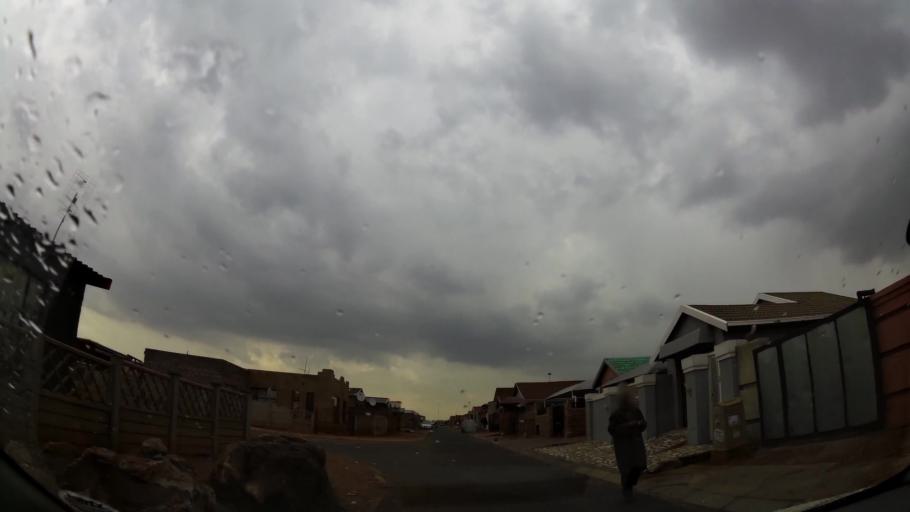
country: ZA
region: Gauteng
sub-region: Ekurhuleni Metropolitan Municipality
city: Germiston
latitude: -26.3698
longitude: 28.1650
